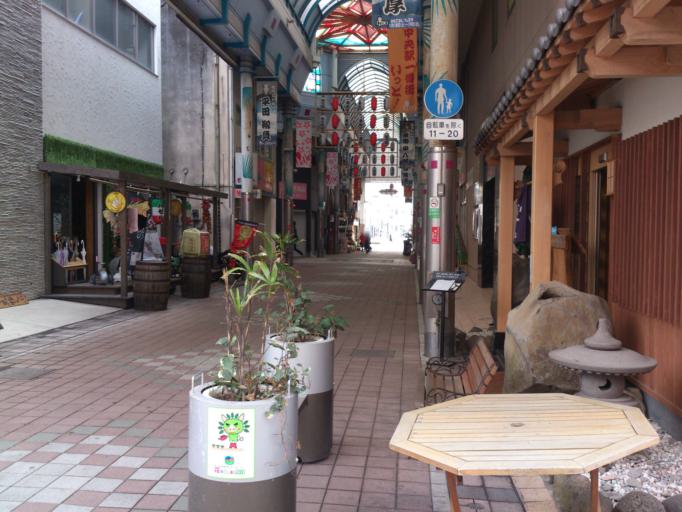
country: JP
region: Kagoshima
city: Kagoshima-shi
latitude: 31.5824
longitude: 130.5425
